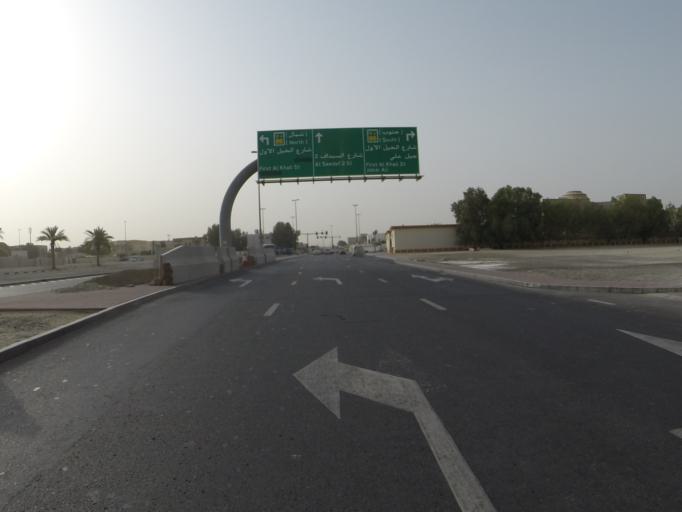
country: AE
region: Dubai
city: Dubai
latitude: 25.1132
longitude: 55.2068
